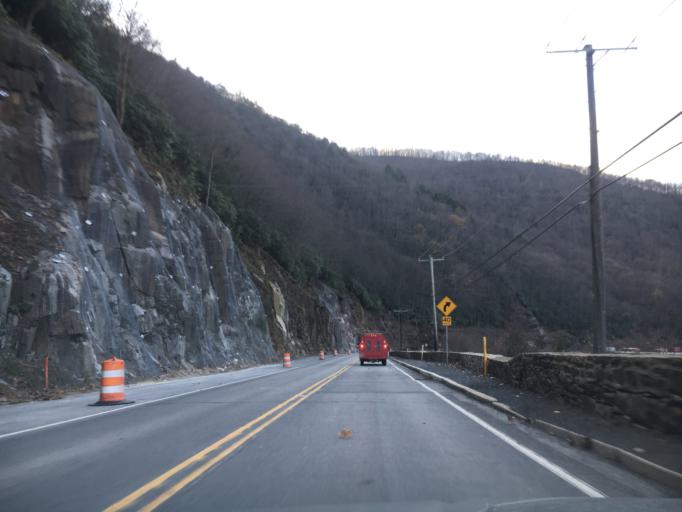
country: US
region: Pennsylvania
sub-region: Carbon County
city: Jim Thorpe
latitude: 40.8588
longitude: -75.7338
